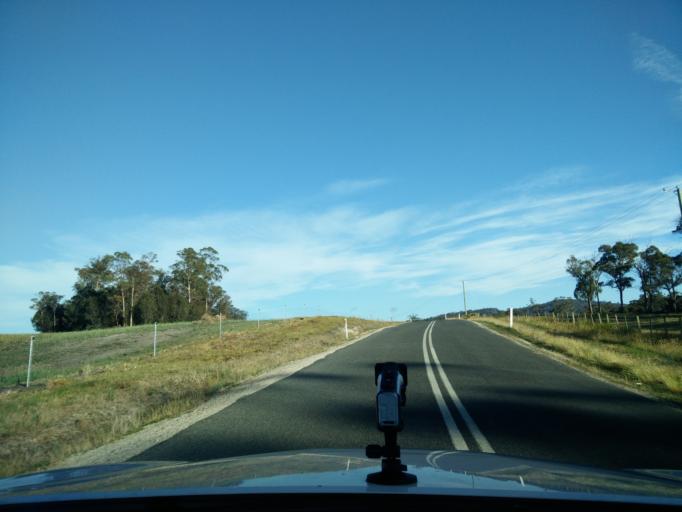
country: AU
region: Tasmania
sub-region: Break O'Day
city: St Helens
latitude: -41.2791
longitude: 148.1258
